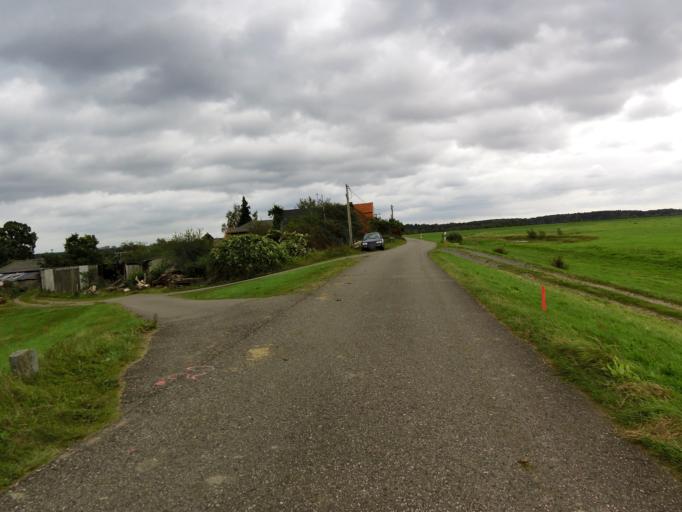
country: DE
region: Saxony-Anhalt
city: Havelberg
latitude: 52.8742
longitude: 12.0250
